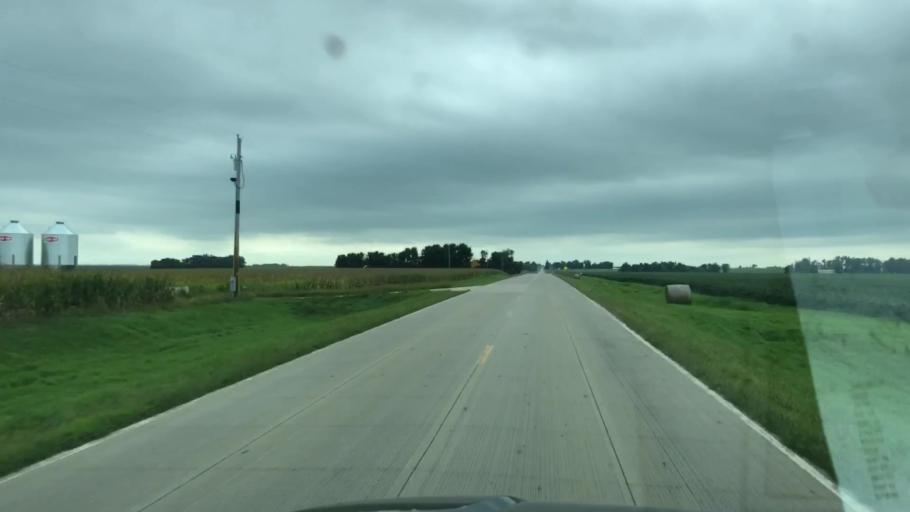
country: US
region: Iowa
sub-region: O'Brien County
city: Sheldon
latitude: 43.1246
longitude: -95.9790
